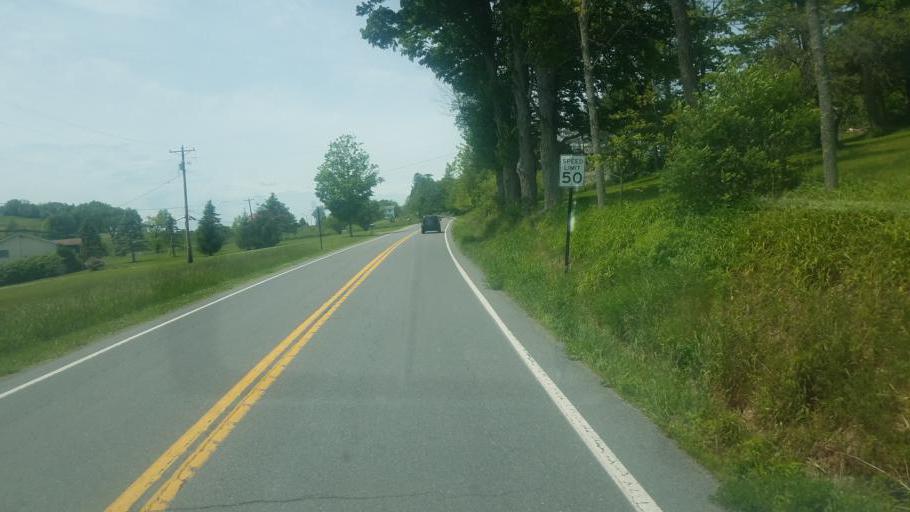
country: US
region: Pennsylvania
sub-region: Tioga County
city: Wellsboro
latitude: 41.7621
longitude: -77.2579
